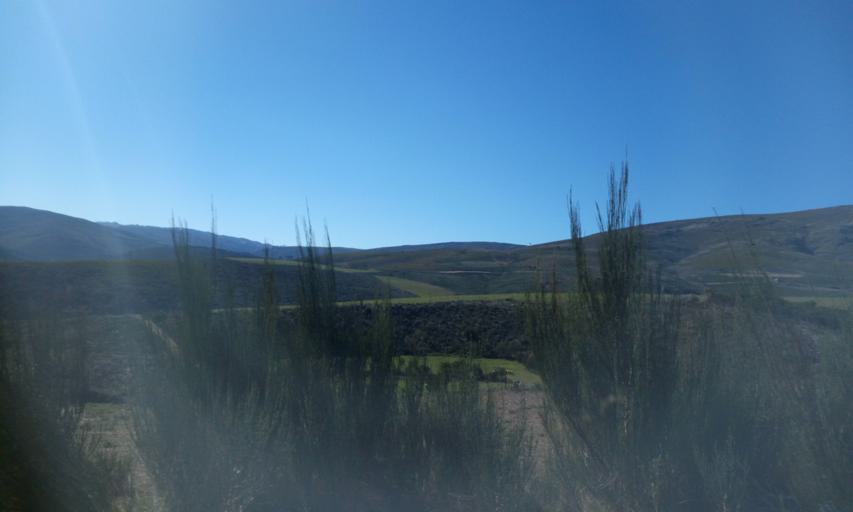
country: PT
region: Guarda
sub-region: Manteigas
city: Manteigas
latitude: 40.4613
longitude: -7.4972
